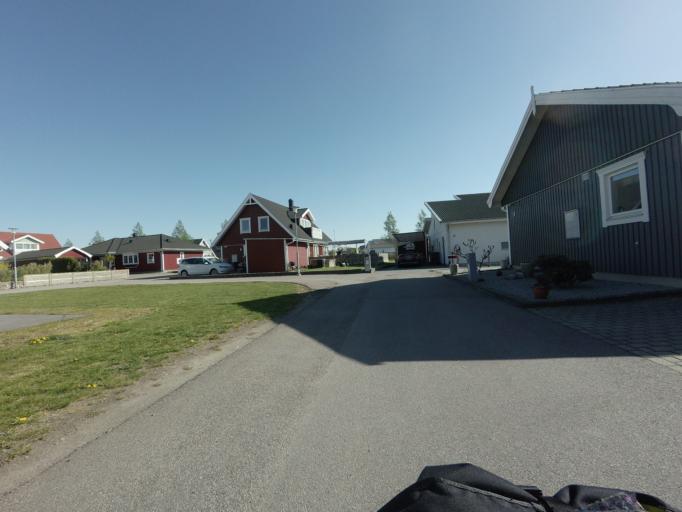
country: SE
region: Skane
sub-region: Landskrona
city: Asmundtorp
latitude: 55.8538
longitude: 12.9082
